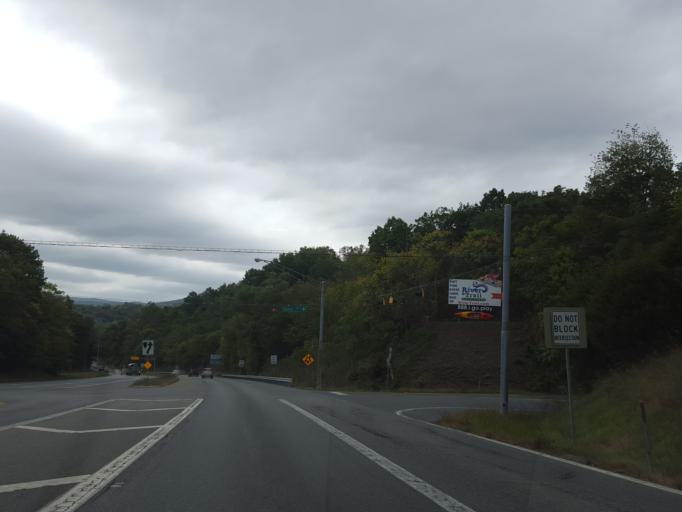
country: US
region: West Virginia
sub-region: Jefferson County
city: Bolivar
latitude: 39.3307
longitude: -77.7026
